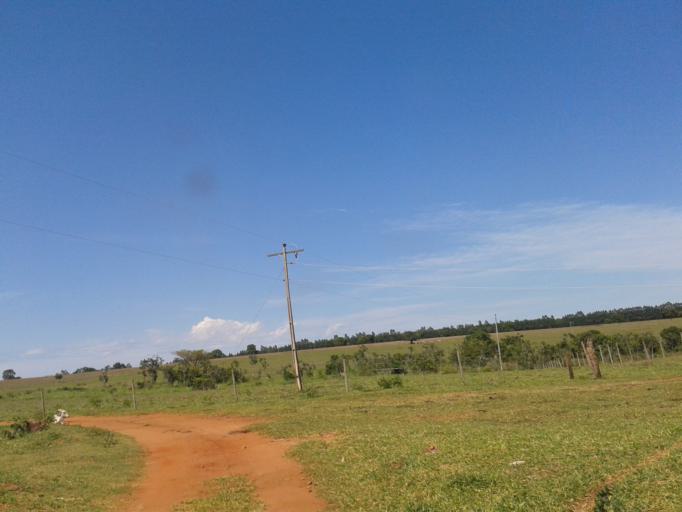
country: BR
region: Minas Gerais
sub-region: Centralina
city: Centralina
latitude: -18.7125
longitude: -49.1559
